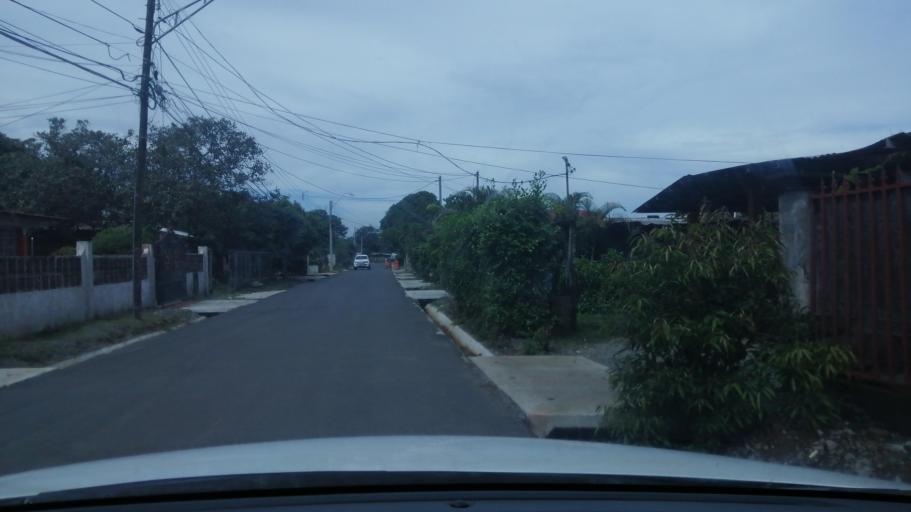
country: PA
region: Chiriqui
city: David
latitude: 8.4176
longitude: -82.4491
